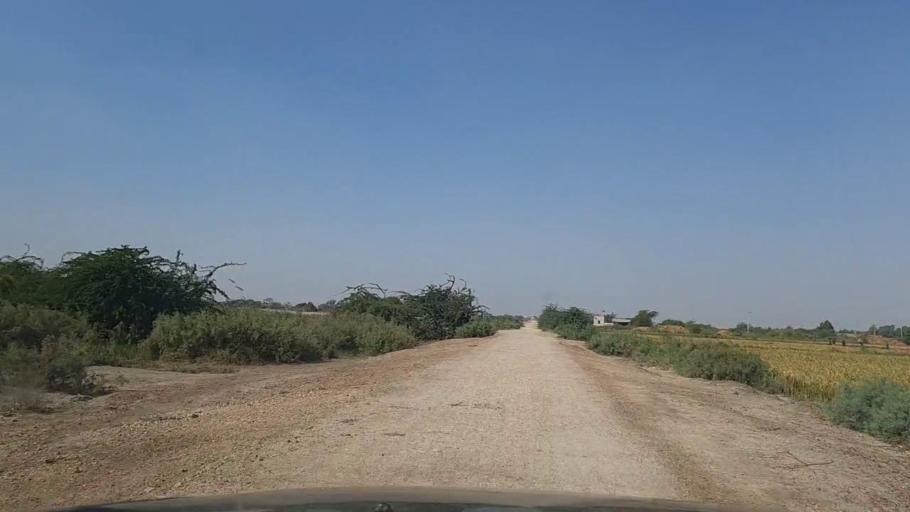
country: PK
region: Sindh
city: Daro Mehar
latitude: 24.8320
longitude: 68.1439
